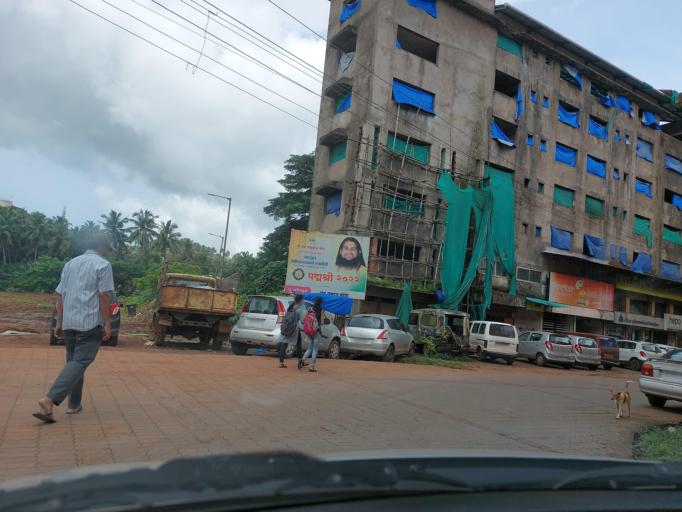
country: IN
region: Goa
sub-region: North Goa
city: Ponda
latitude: 15.3971
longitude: 74.0026
